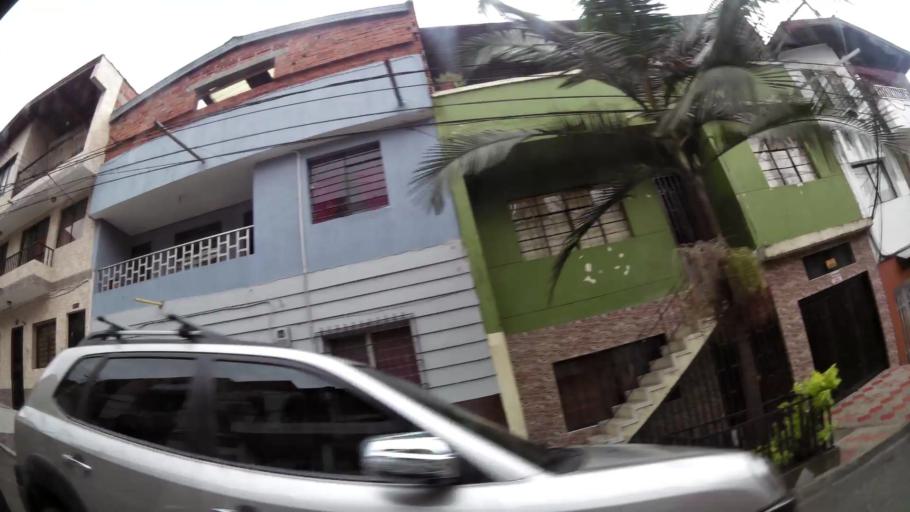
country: CO
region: Antioquia
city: Medellin
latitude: 6.2361
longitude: -75.5611
